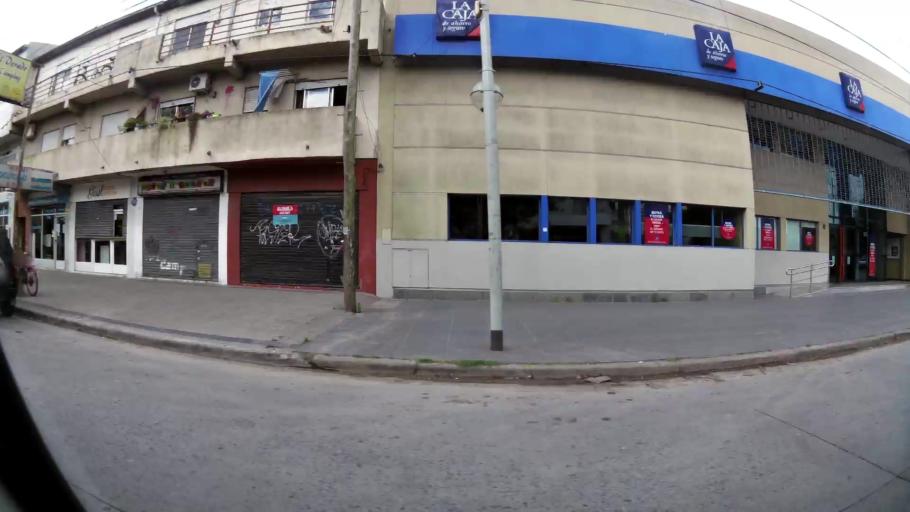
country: AR
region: Buenos Aires
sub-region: Partido de La Plata
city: La Plata
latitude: -34.9093
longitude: -57.9241
